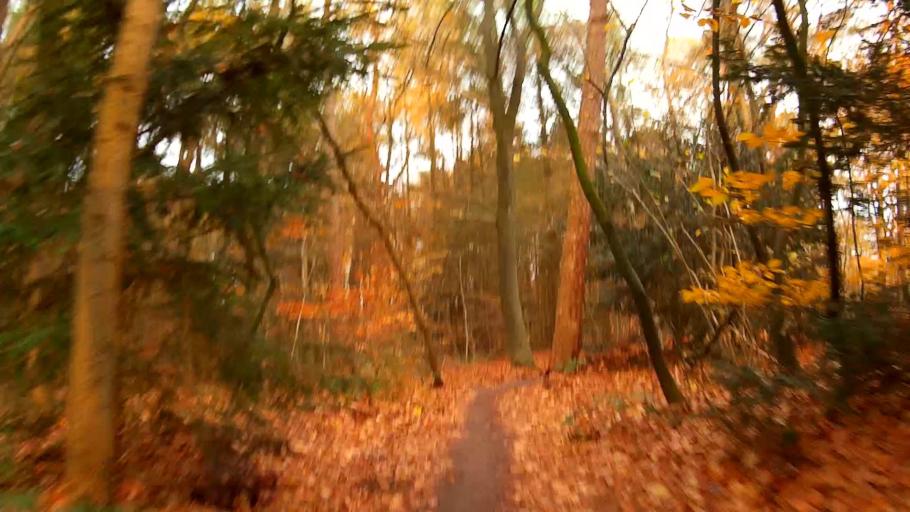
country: NL
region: Utrecht
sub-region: Gemeente Utrechtse Heuvelrug
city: Driebergen-Rijsenburg
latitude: 52.0917
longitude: 5.2790
